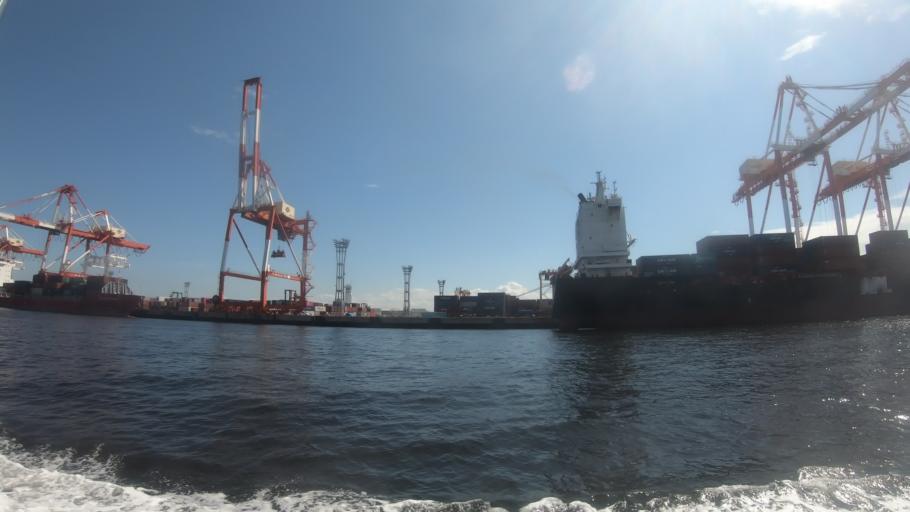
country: JP
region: Kanagawa
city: Yokohama
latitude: 35.4392
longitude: 139.6819
